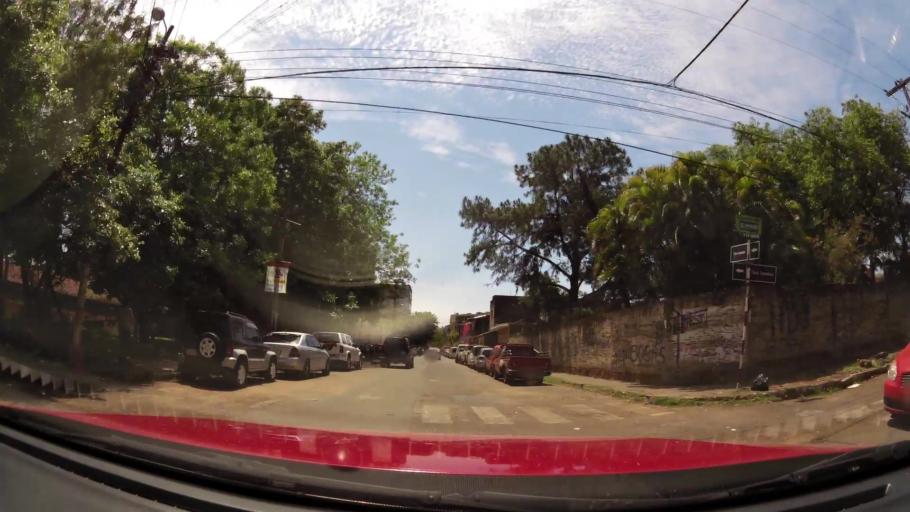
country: PY
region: Central
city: San Lorenzo
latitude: -25.3430
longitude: -57.5116
